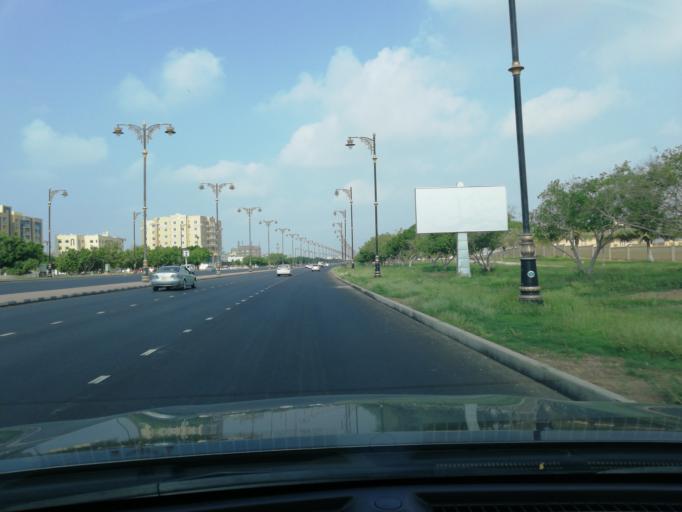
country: OM
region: Zufar
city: Salalah
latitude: 17.0235
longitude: 54.0859
